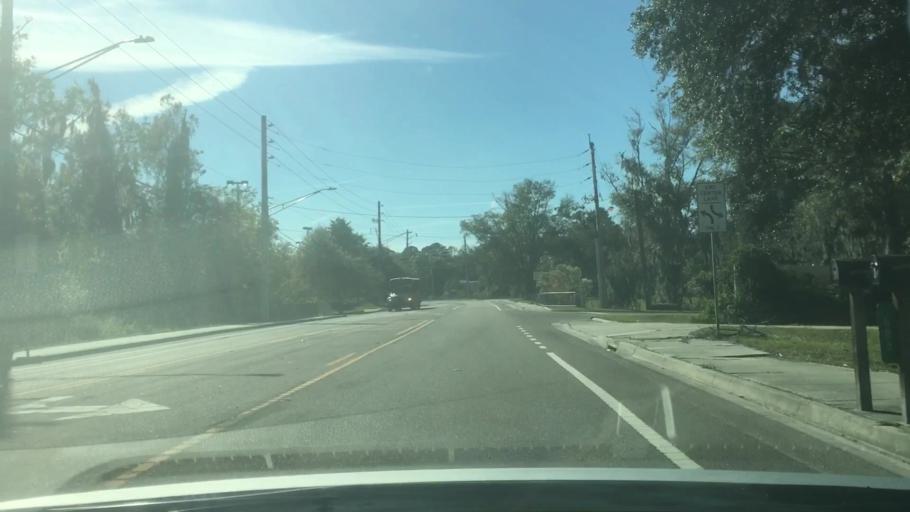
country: US
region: Florida
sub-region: Duval County
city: Jacksonville
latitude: 30.4702
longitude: -81.6164
